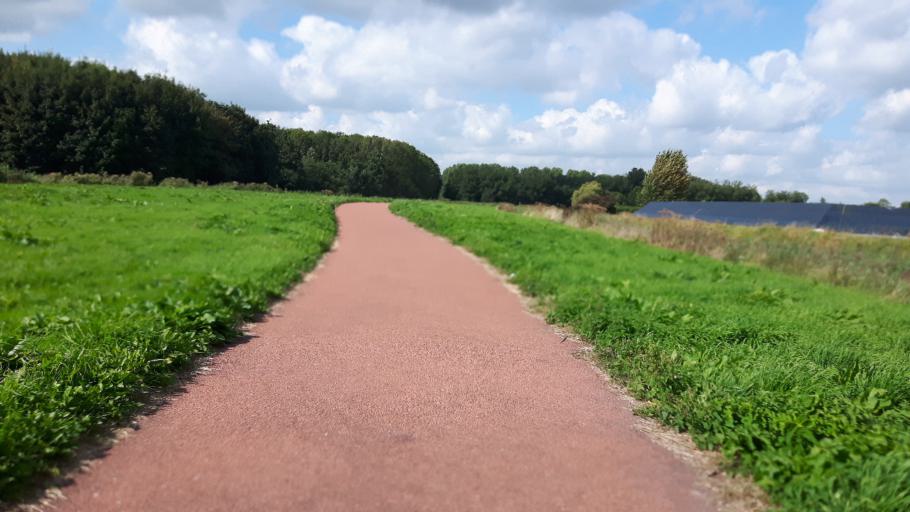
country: NL
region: North Holland
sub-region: Gemeente Enkhuizen
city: Enkhuizen
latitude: 52.7171
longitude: 5.2388
